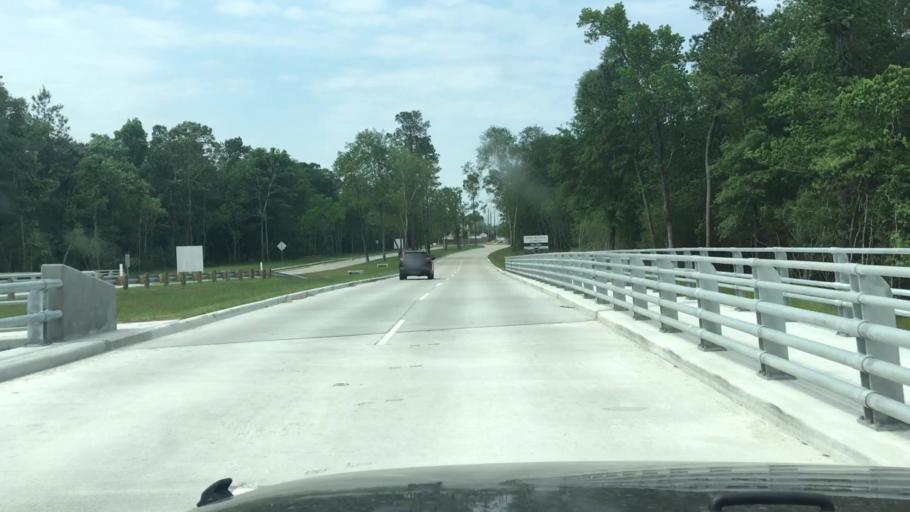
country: US
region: Texas
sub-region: Harris County
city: Atascocita
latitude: 29.9612
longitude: -95.2099
